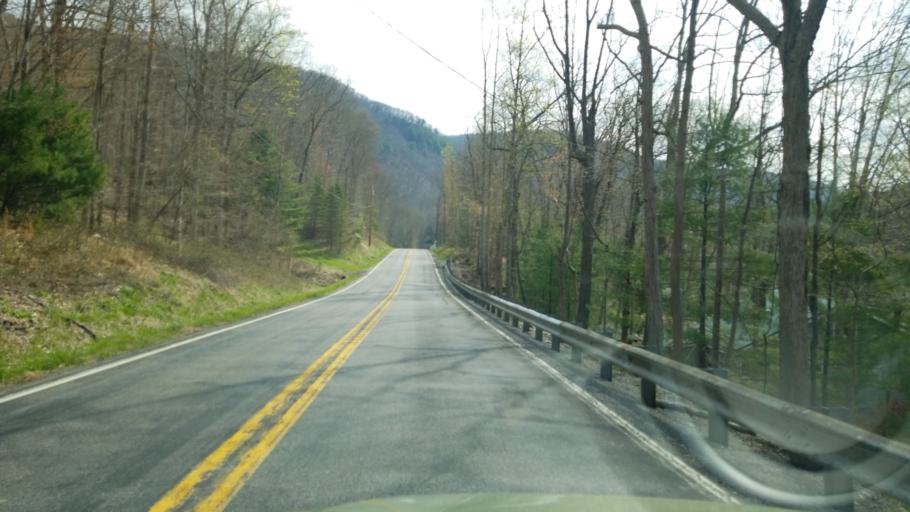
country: US
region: Pennsylvania
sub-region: Clinton County
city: Renovo
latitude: 41.3003
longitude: -77.9941
